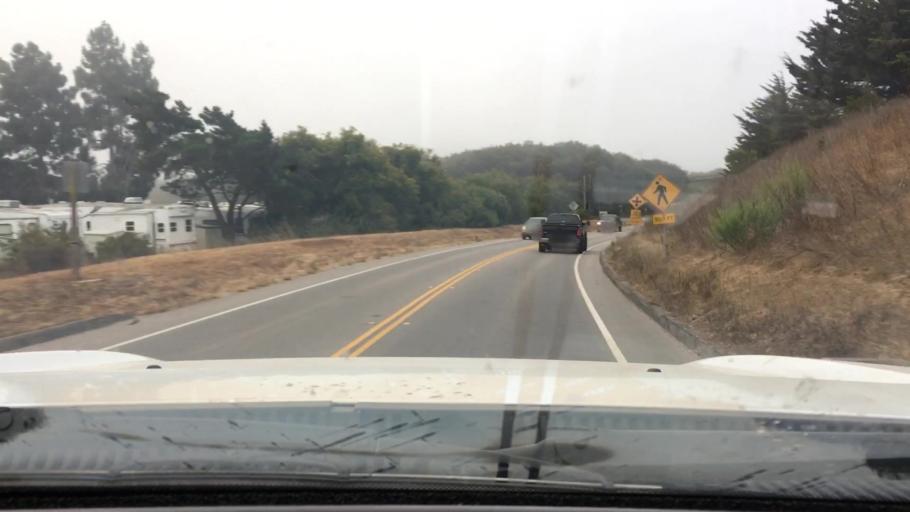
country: US
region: California
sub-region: San Luis Obispo County
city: Morro Bay
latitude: 35.3646
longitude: -120.8264
